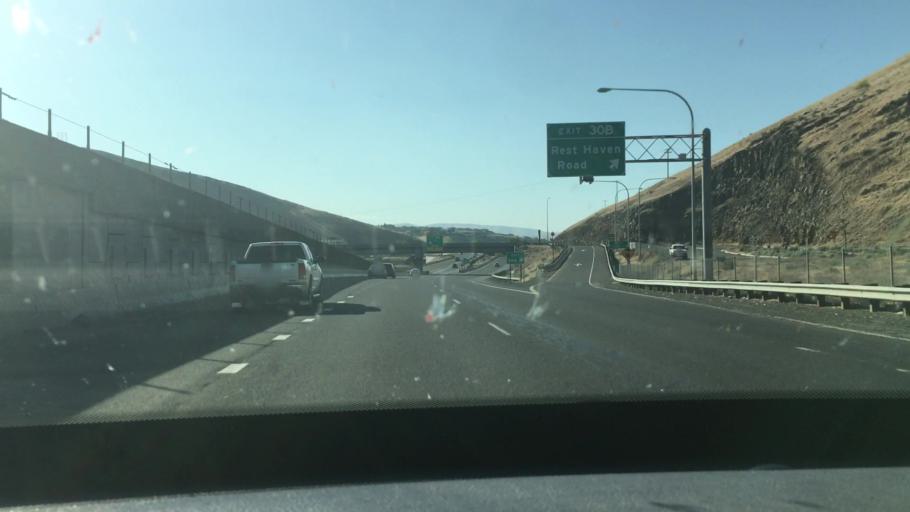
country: US
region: Washington
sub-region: Yakima County
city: Selah
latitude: 46.6318
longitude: -120.5175
